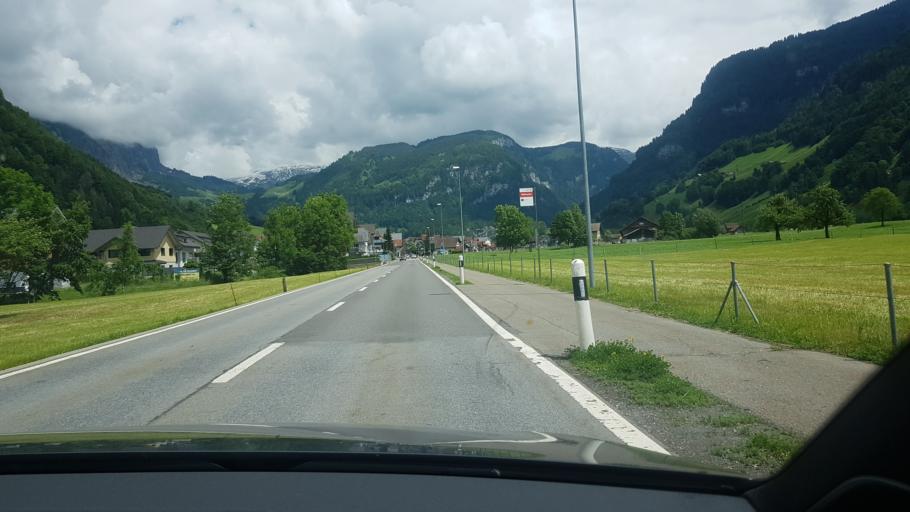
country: CH
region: Schwyz
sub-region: Bezirk Schwyz
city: Muotathal
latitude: 46.9758
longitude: 8.7467
